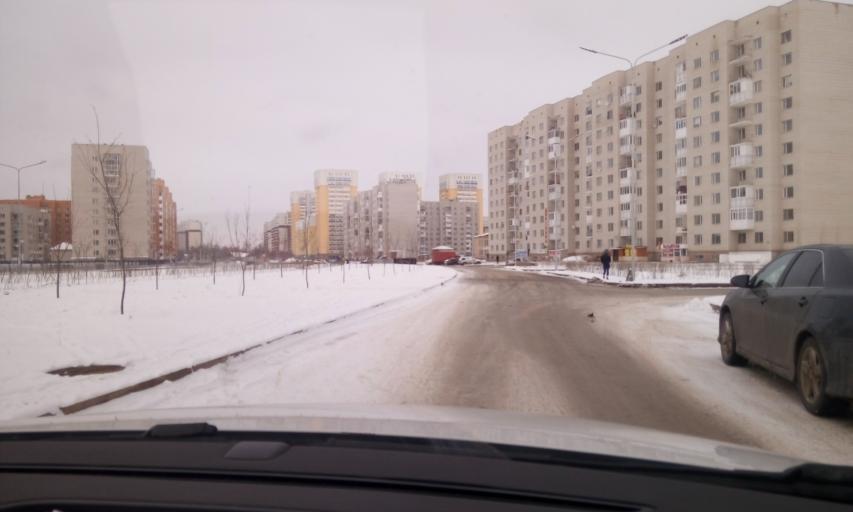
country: KZ
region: Astana Qalasy
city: Astana
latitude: 51.1246
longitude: 71.5052
